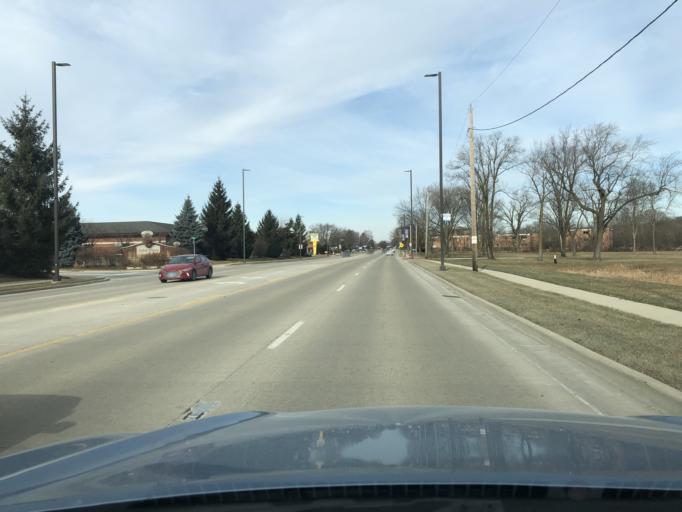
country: US
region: Illinois
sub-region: Cook County
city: Wheeling
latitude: 42.1300
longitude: -87.9000
